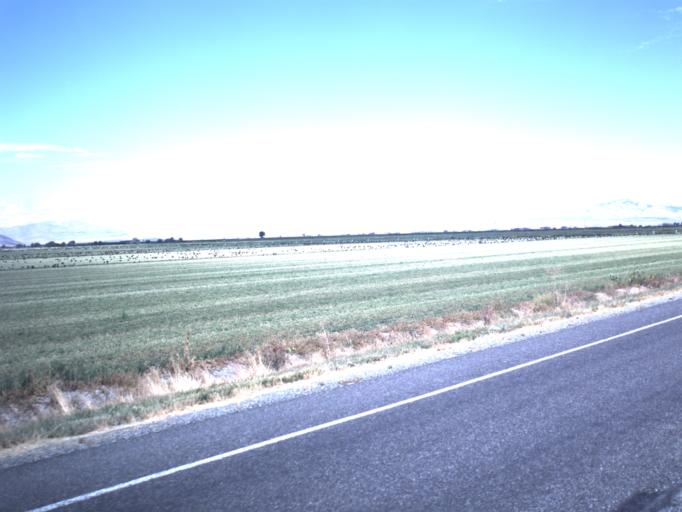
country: US
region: Utah
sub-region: Box Elder County
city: Honeyville
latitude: 41.5710
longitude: -112.1297
